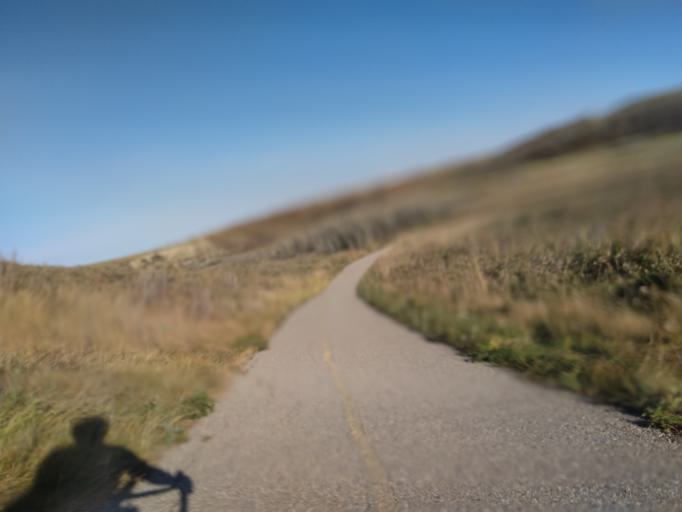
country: CA
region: Alberta
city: Calgary
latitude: 51.1326
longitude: -114.0608
